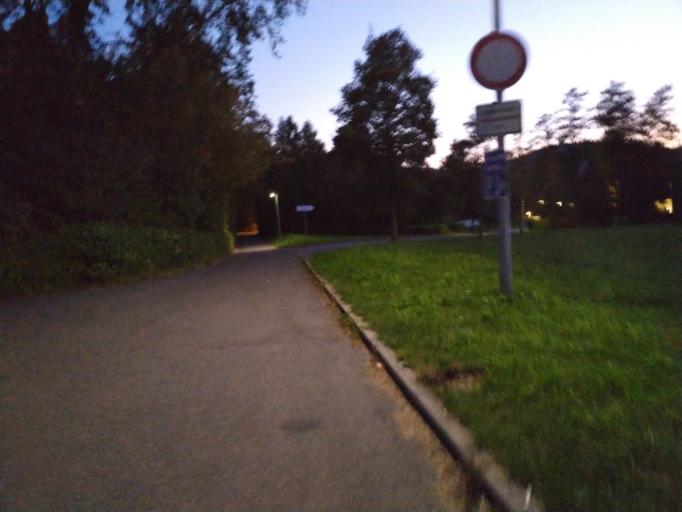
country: DE
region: Baden-Wuerttemberg
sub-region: Regierungsbezirk Stuttgart
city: Boll
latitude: 48.6394
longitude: 9.6018
